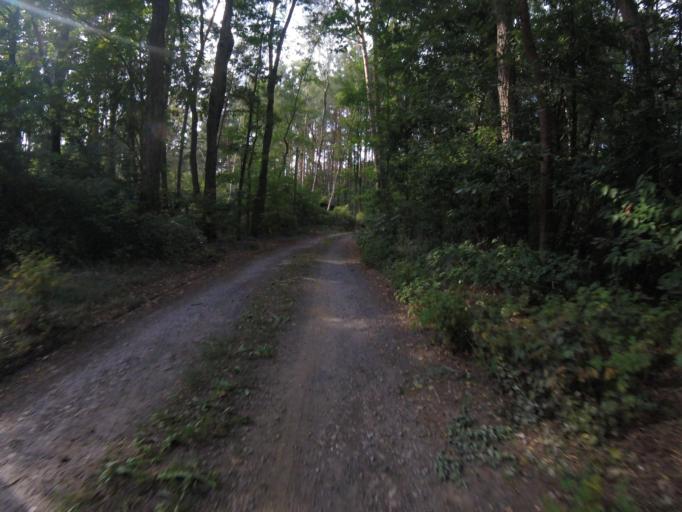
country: DE
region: Brandenburg
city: Munchehofe
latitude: 52.2514
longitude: 13.7843
